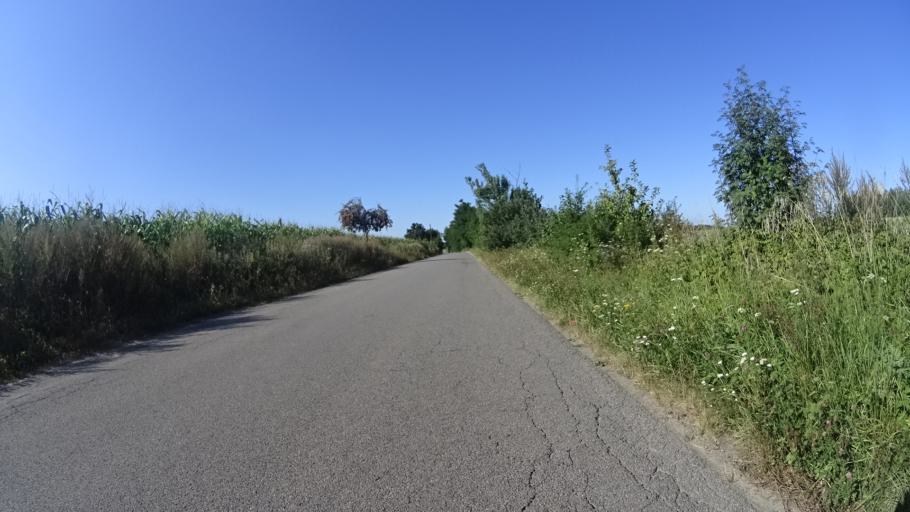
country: PL
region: Masovian Voivodeship
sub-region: Powiat bialobrzeski
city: Wysmierzyce
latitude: 51.6690
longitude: 20.8313
